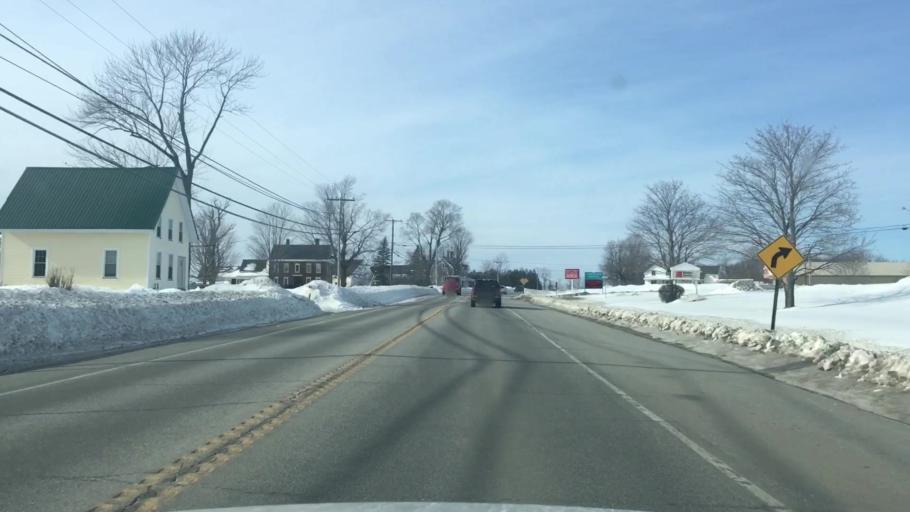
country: US
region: Maine
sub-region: Penobscot County
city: Charleston
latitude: 44.9910
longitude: -69.0164
